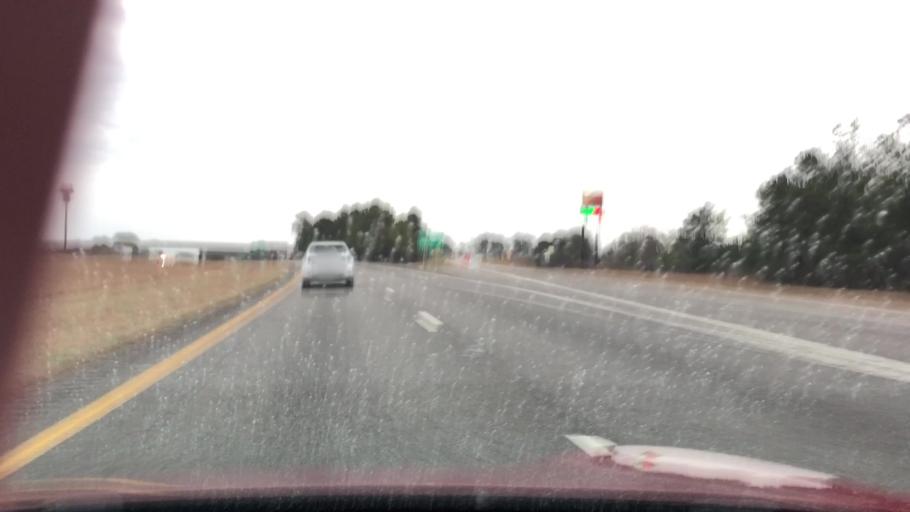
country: US
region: South Carolina
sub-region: Dillon County
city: Latta
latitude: 34.3403
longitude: -79.5370
